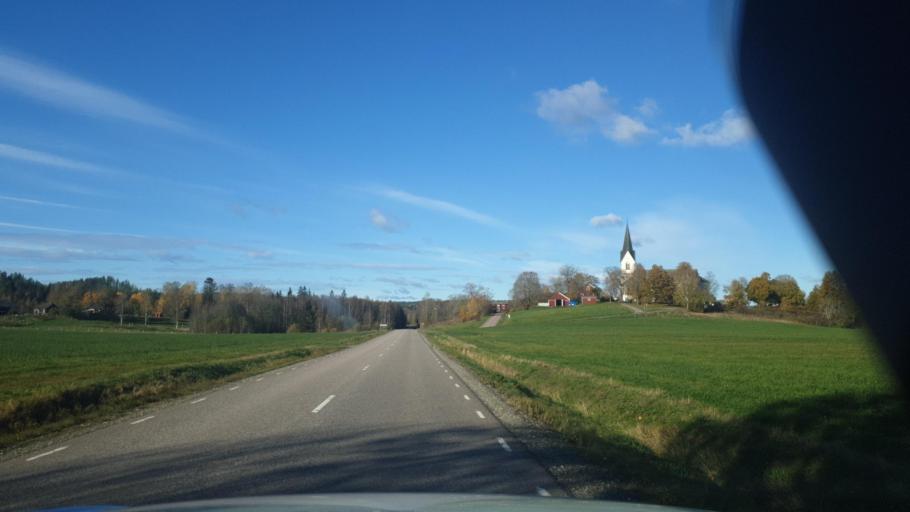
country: SE
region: Vaermland
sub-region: Arvika Kommun
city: Arvika
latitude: 59.6500
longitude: 12.8918
